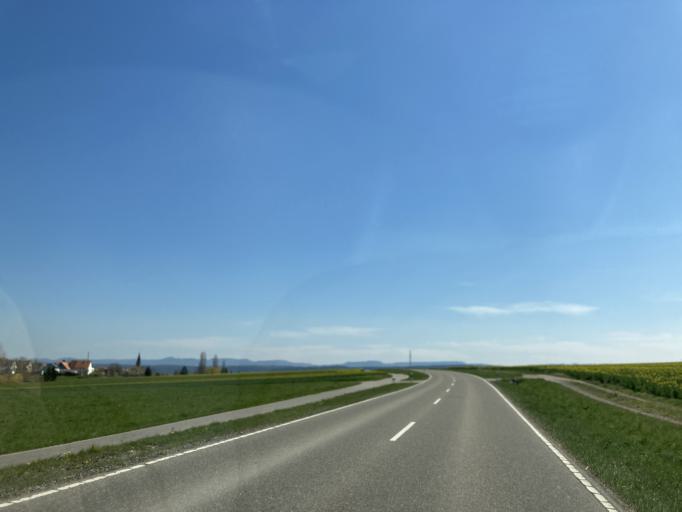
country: DE
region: Baden-Wuerttemberg
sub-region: Tuebingen Region
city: Rottenburg
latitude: 48.5105
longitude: 8.9267
